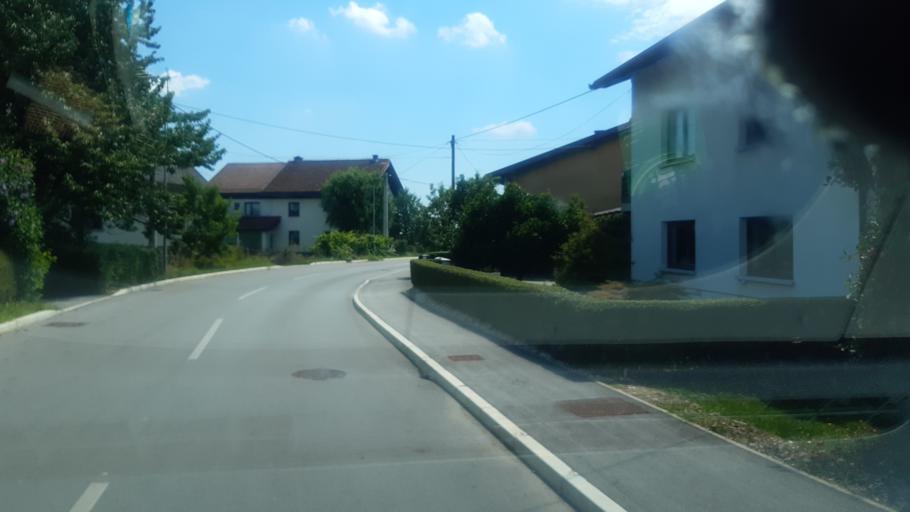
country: SI
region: Moravske Toplice
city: Moravske Toplice
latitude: 46.6824
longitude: 16.1939
